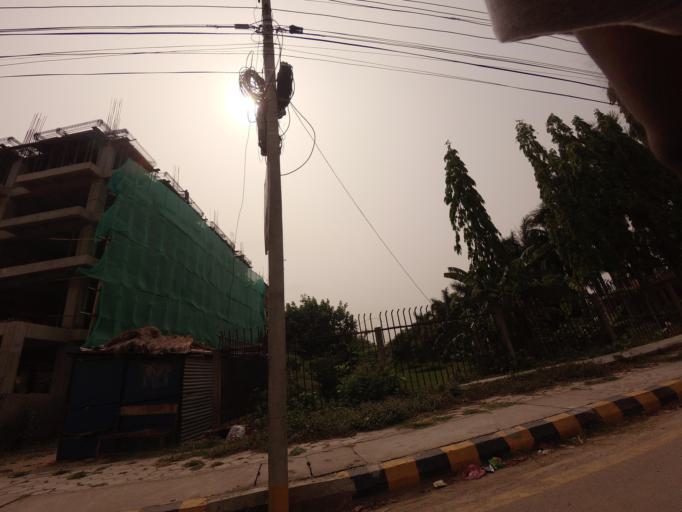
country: IN
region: Uttar Pradesh
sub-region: Maharajganj
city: Nautanwa
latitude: 27.4690
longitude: 83.2839
